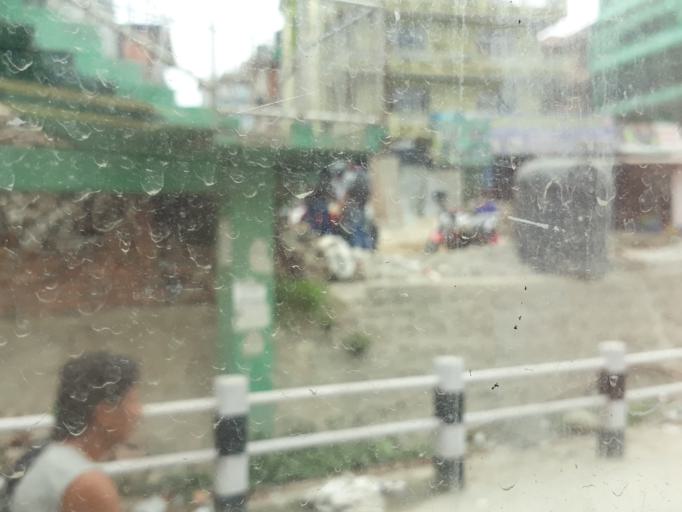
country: NP
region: Central Region
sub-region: Bagmati Zone
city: Patan
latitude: 27.6748
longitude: 85.3604
